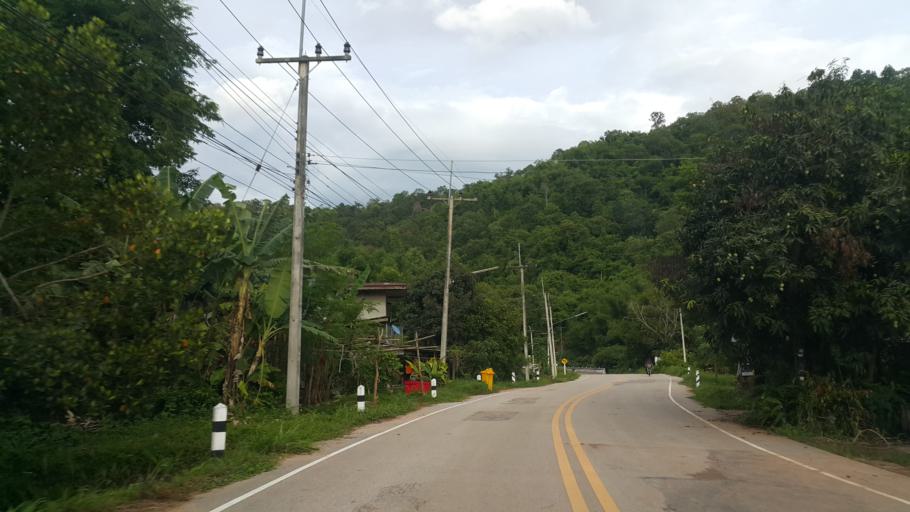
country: TH
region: Loei
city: Na Haeo
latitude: 17.4992
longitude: 101.0787
